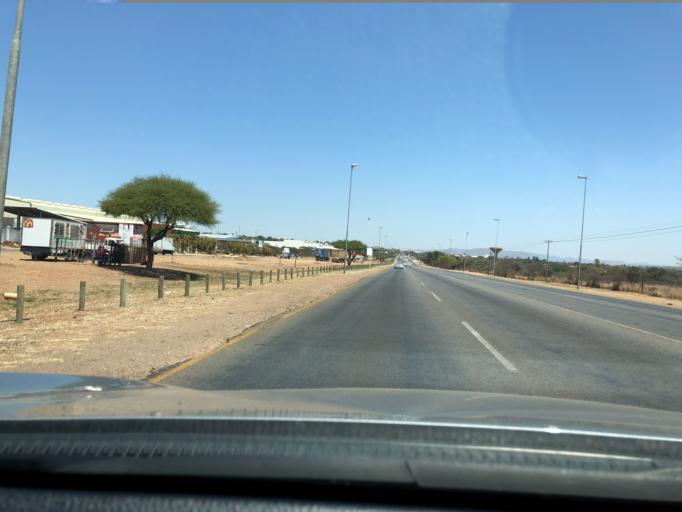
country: ZA
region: Limpopo
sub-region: Capricorn District Municipality
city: Polokwane
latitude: -23.8648
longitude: 29.4688
